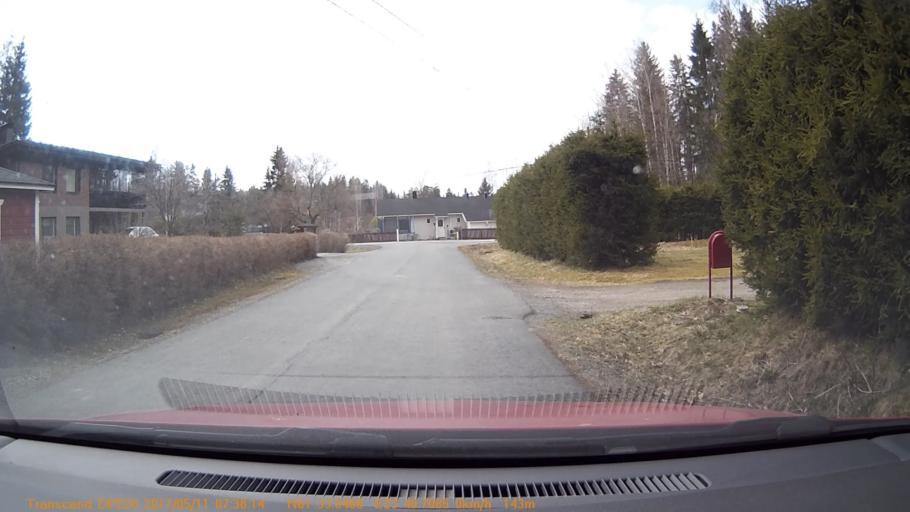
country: FI
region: Pirkanmaa
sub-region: Tampere
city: Yloejaervi
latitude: 61.5508
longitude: 23.6785
